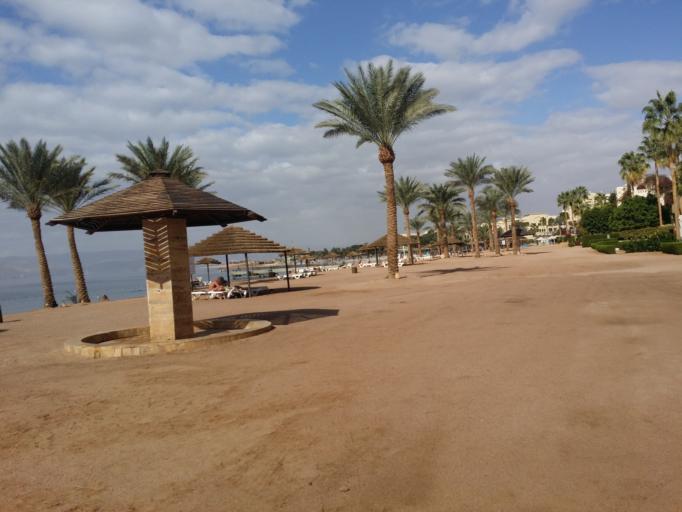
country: JO
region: Aqaba
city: Aqaba
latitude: 29.4097
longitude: 34.9781
